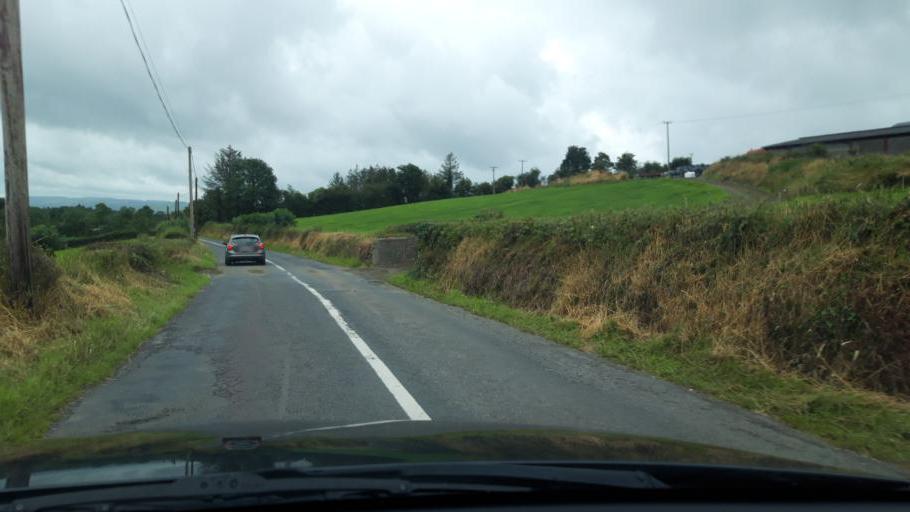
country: IE
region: Munster
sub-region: County Cork
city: Youghal
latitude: 52.1634
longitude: -7.8488
